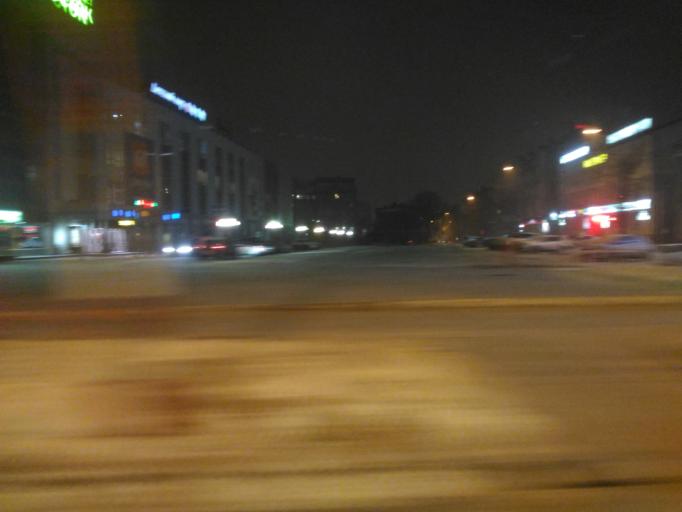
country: RU
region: Ulyanovsk
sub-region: Ulyanovskiy Rayon
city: Ulyanovsk
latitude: 54.3278
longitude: 48.4026
